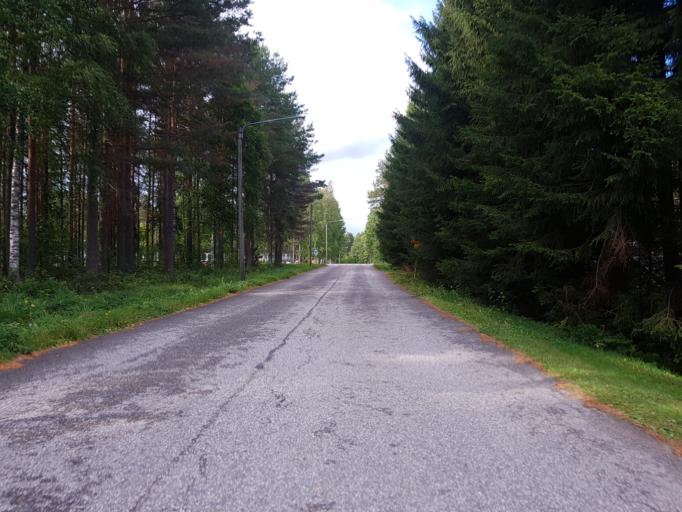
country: FI
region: Kainuu
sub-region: Kehys-Kainuu
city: Kuhmo
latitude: 64.1250
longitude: 29.5375
